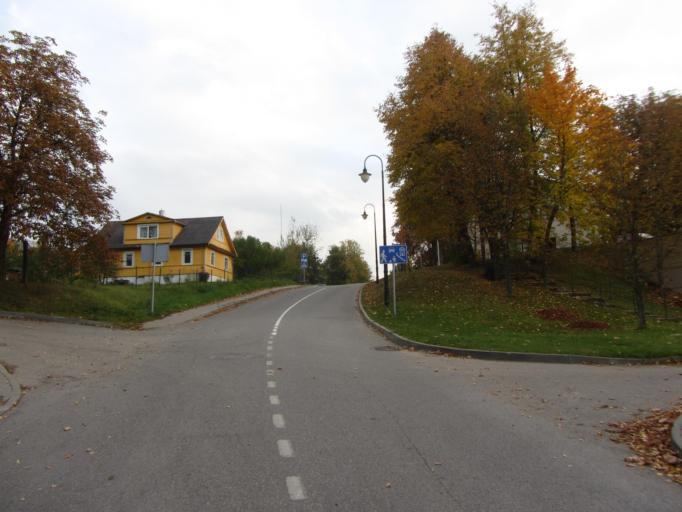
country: LT
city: Trakai
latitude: 54.6392
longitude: 24.9388
